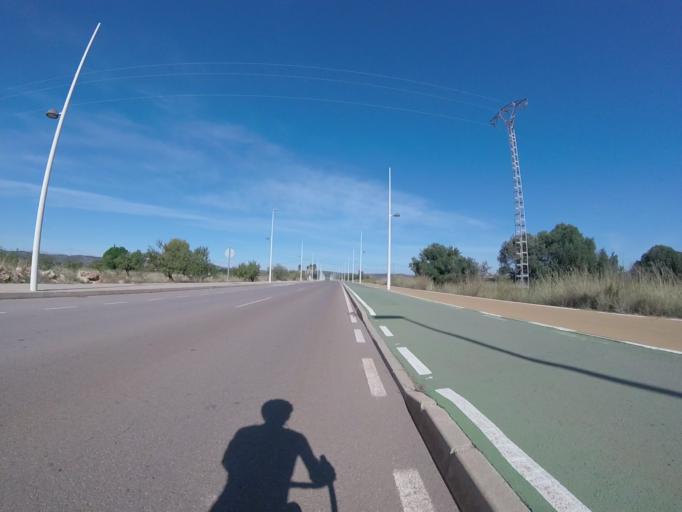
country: ES
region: Valencia
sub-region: Provincia de Castello
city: Torreblanca
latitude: 40.2114
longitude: 0.2240
